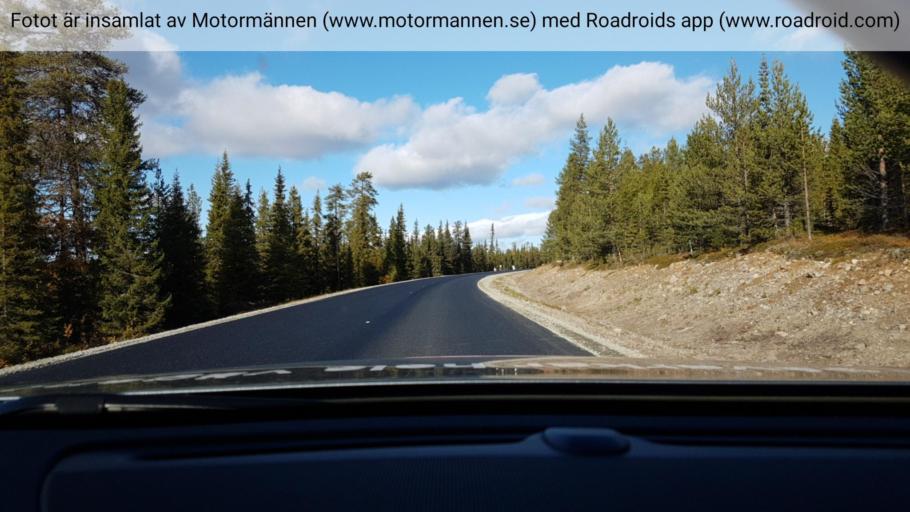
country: SE
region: Norrbotten
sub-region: Arjeplogs Kommun
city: Arjeplog
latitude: 65.9197
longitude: 18.3183
